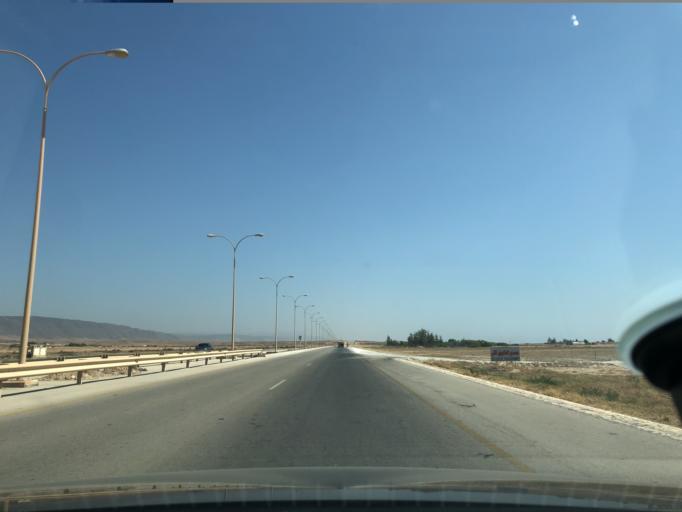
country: OM
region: Zufar
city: Salalah
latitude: 17.0524
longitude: 54.2898
